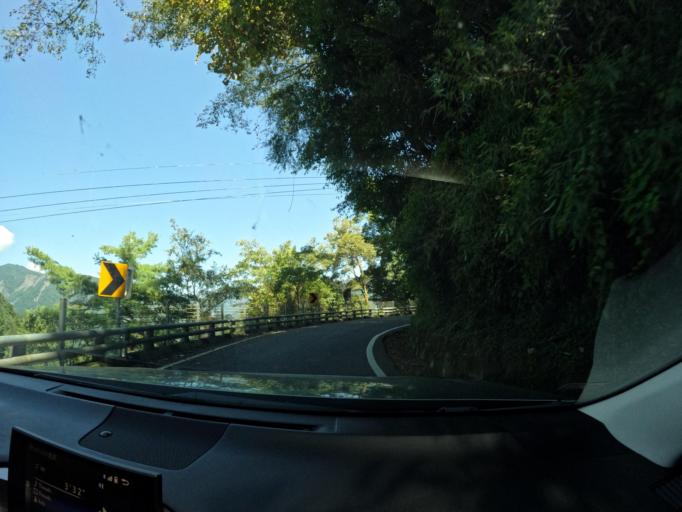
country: TW
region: Taiwan
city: Yujing
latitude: 23.2850
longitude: 120.9002
